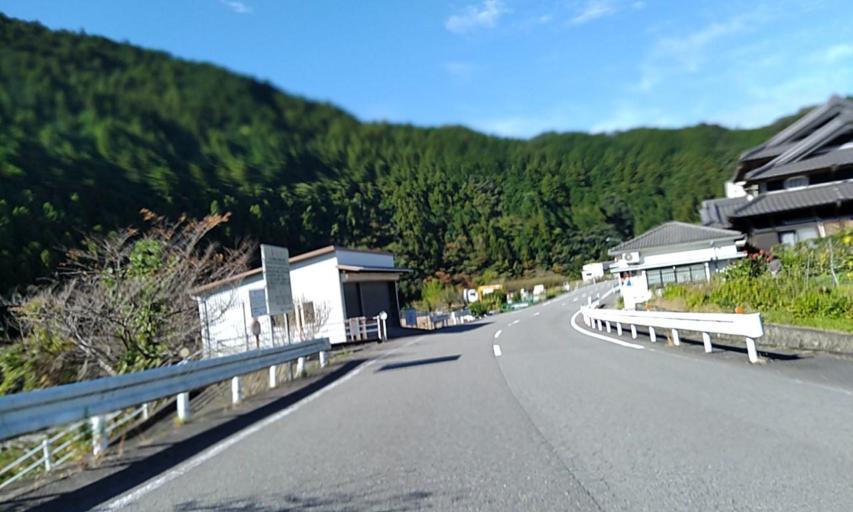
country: JP
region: Wakayama
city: Kainan
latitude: 34.0467
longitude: 135.3386
